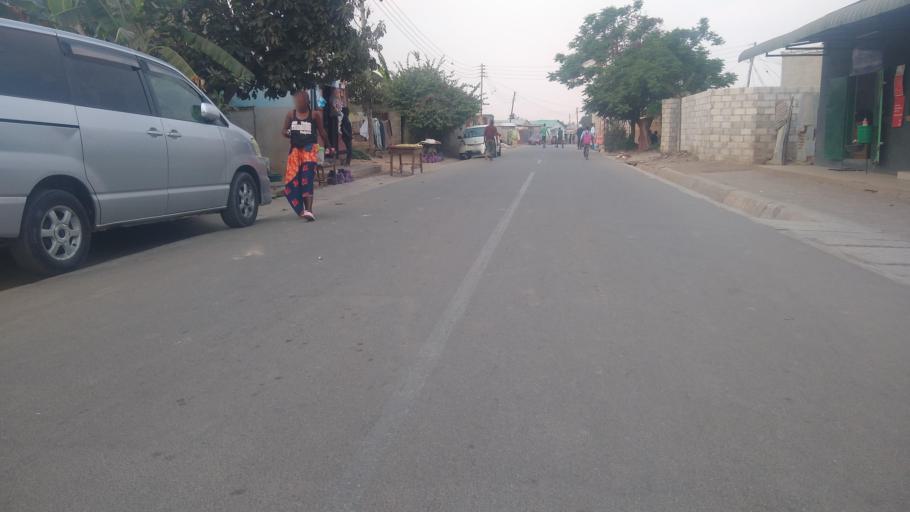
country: ZM
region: Lusaka
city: Lusaka
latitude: -15.4459
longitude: 28.3742
